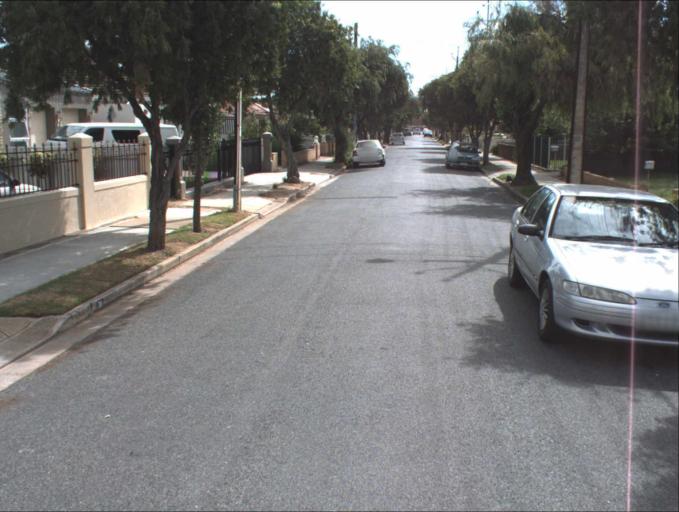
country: AU
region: South Australia
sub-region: Port Adelaide Enfield
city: Blair Athol
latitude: -34.8683
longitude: 138.5870
